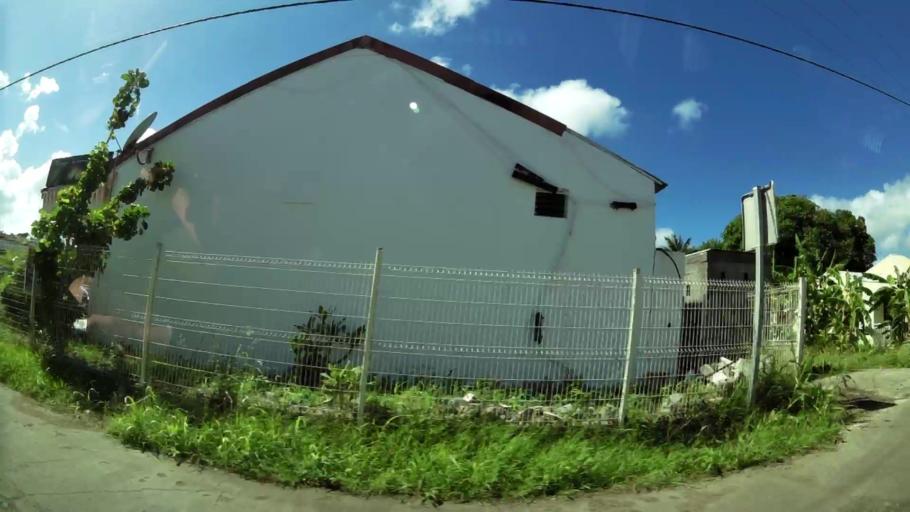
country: GP
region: Guadeloupe
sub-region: Guadeloupe
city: Petit-Canal
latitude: 16.3914
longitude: -61.4607
